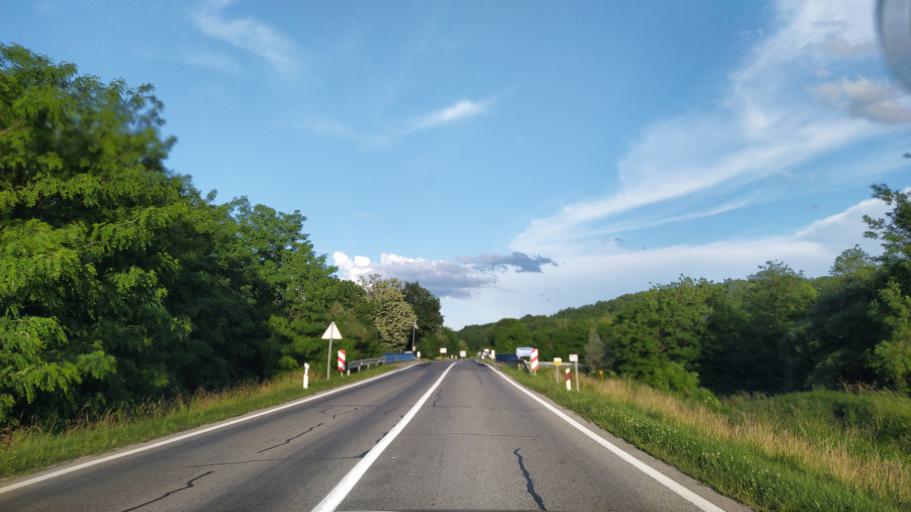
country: HR
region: Virovitick-Podravska
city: Cacinci
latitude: 45.6014
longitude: 17.8336
